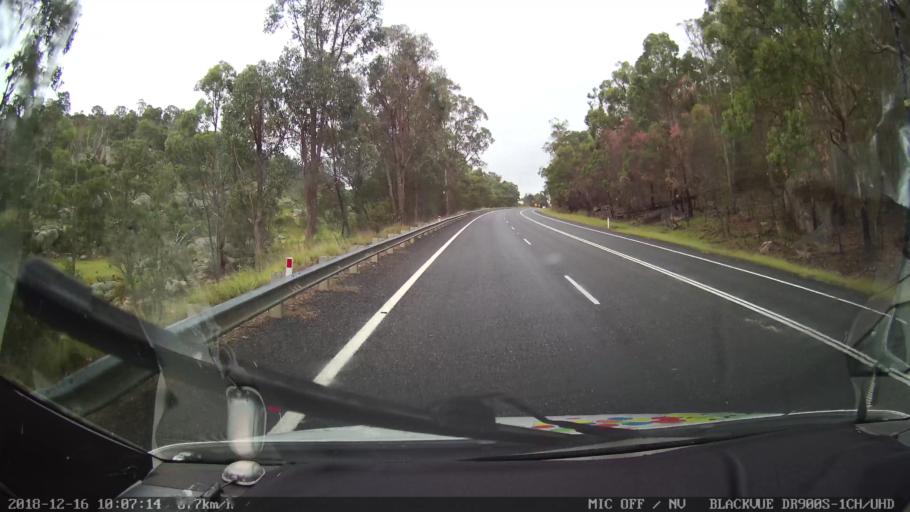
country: AU
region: New South Wales
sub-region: Glen Innes Severn
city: Glen Innes
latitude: -29.3368
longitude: 151.8947
